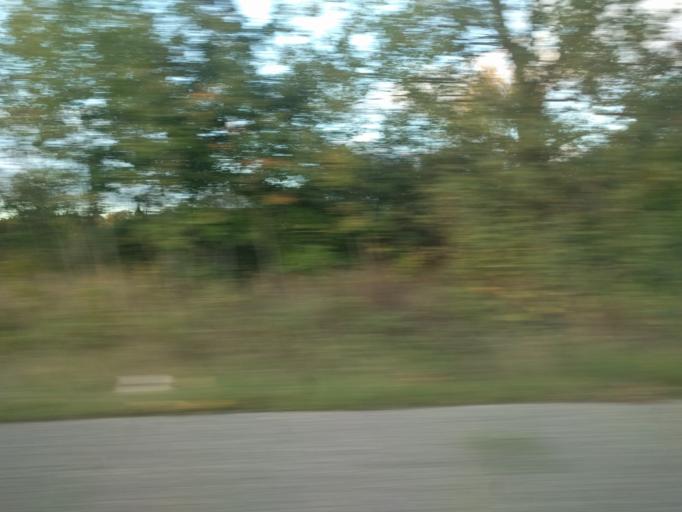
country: DK
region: South Denmark
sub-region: Nyborg Kommune
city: Nyborg
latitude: 55.3363
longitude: 10.7393
